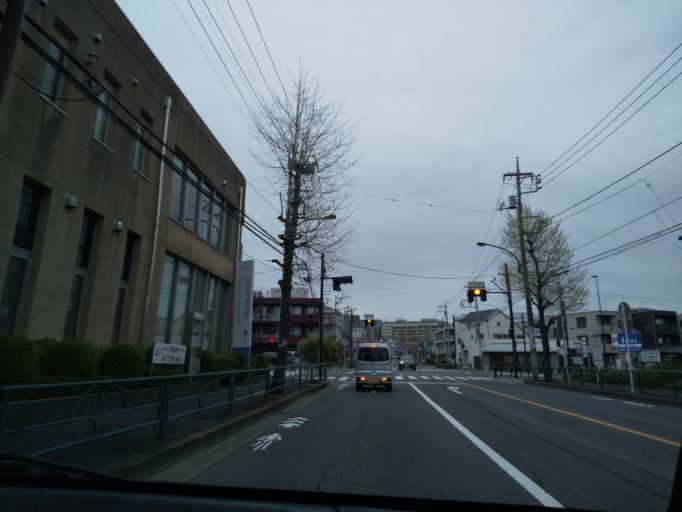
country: JP
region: Tokyo
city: Hino
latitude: 35.6547
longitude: 139.3791
